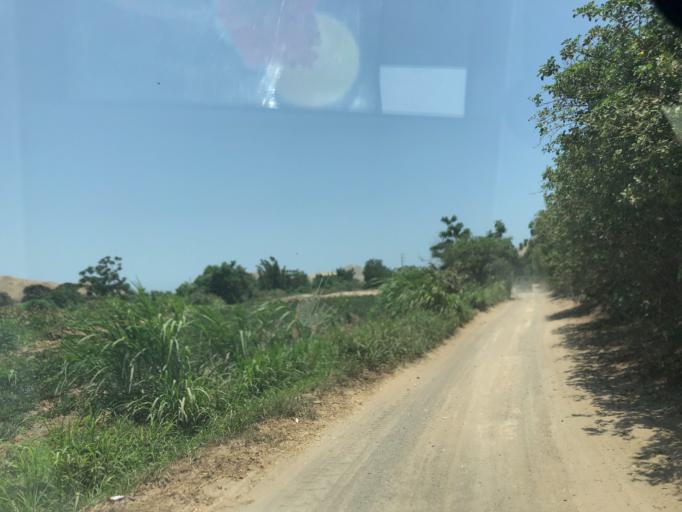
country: PE
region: Lima
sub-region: Provincia de Canete
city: Quilmana
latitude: -13.0013
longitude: -76.4479
